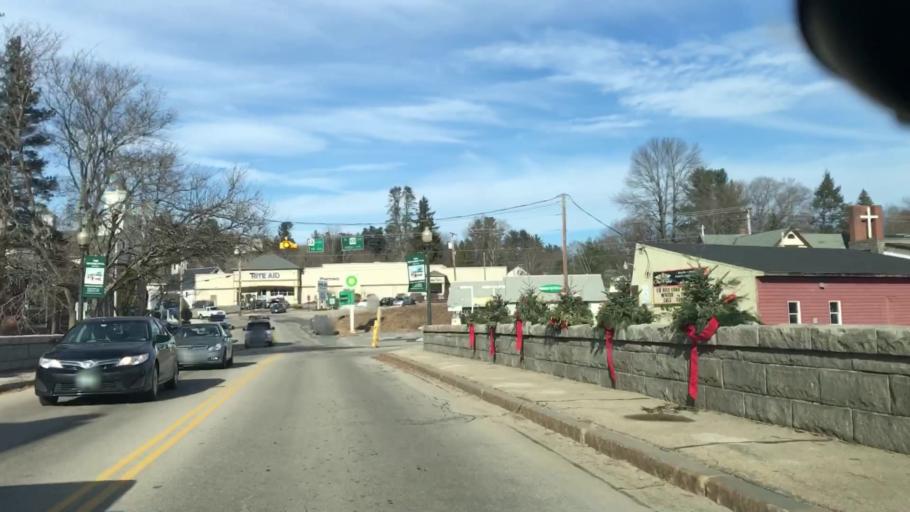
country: US
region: New Hampshire
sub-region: Hillsborough County
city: Milford
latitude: 42.8366
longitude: -71.6495
